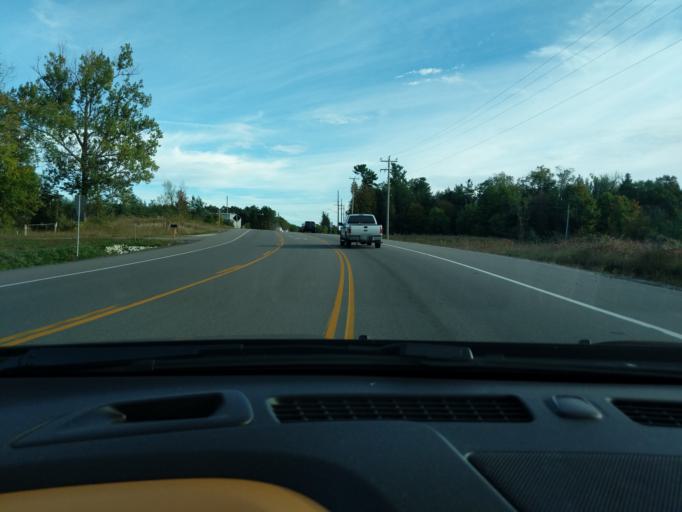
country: CA
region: Ontario
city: Barrie
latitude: 44.4266
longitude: -79.7644
